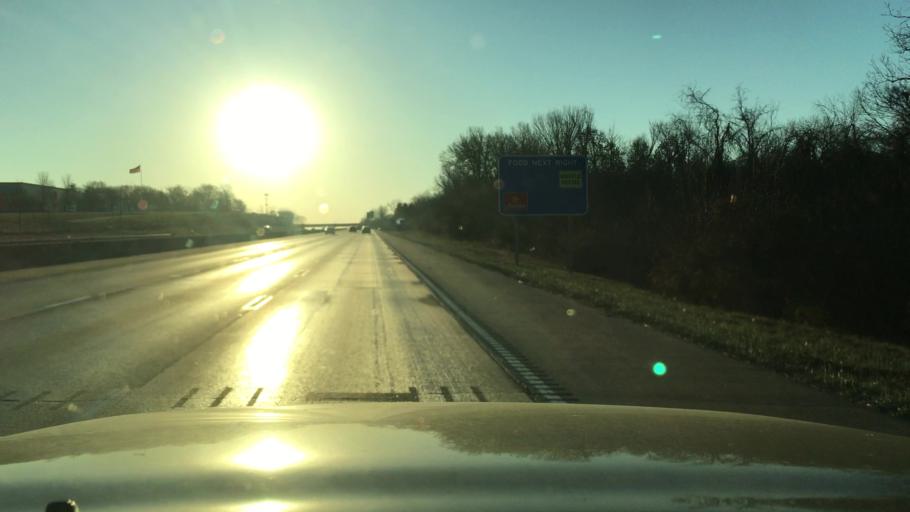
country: US
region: Missouri
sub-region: Saint Charles County
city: Saint Charles
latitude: 38.8117
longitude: -90.4886
